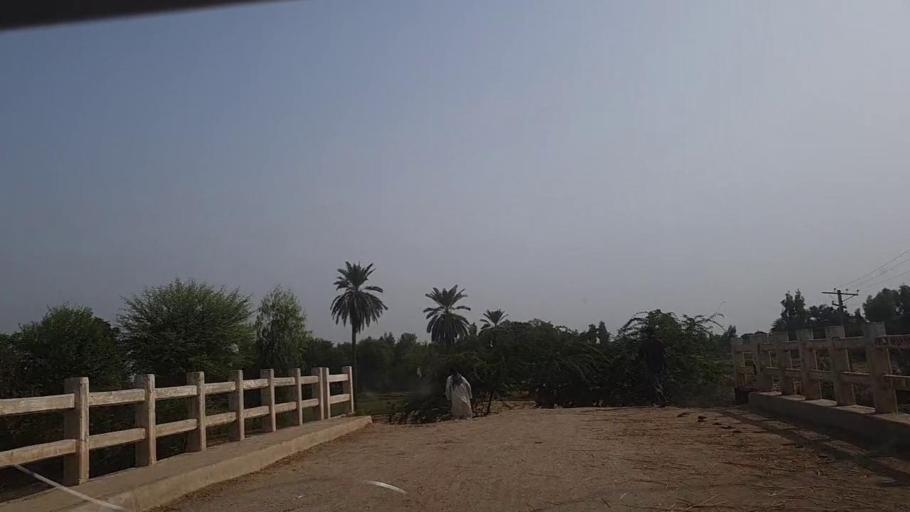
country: PK
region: Sindh
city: Madeji
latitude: 27.7326
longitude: 68.4364
